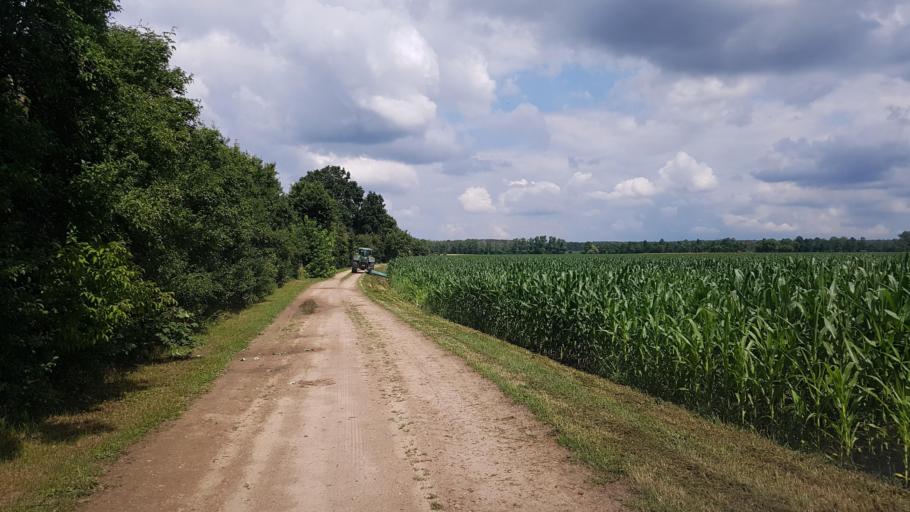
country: DE
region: Brandenburg
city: Sonnewalde
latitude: 51.7003
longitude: 13.7081
